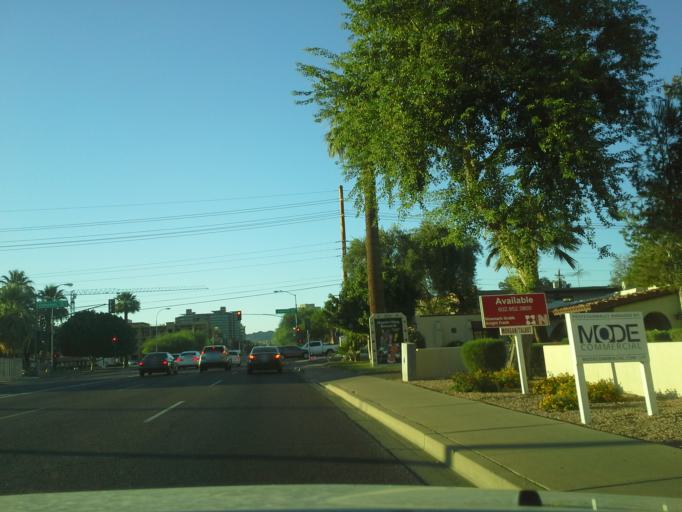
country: US
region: Arizona
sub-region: Maricopa County
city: Phoenix
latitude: 33.5014
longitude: -112.0301
